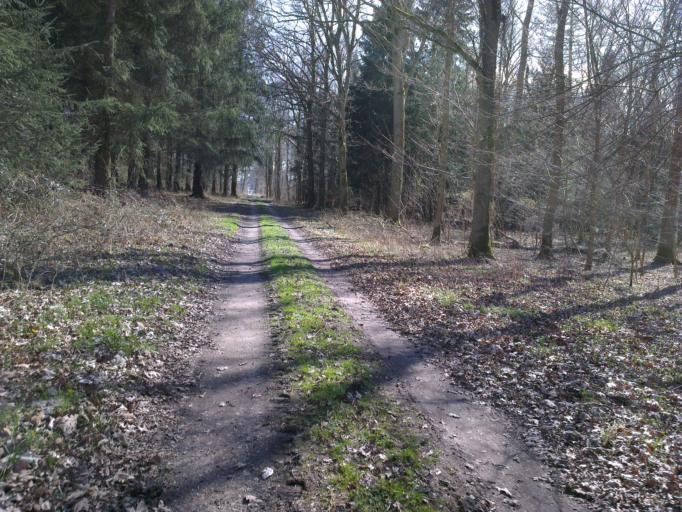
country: DK
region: Capital Region
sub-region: Frederikssund Kommune
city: Jaegerspris
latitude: 55.8890
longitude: 11.9994
